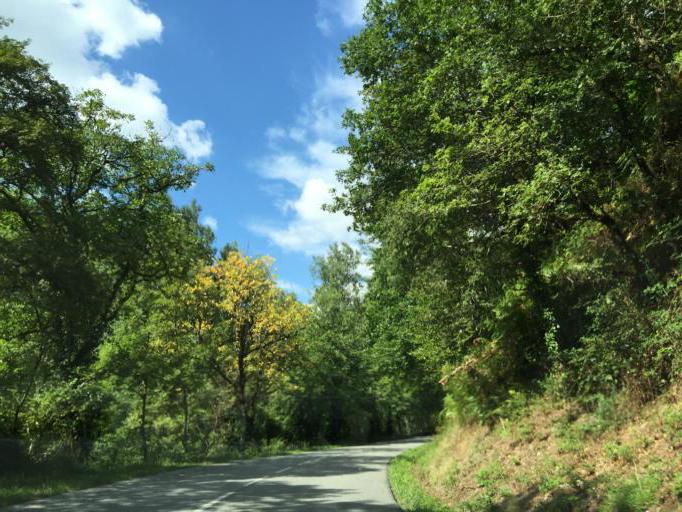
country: FR
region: Midi-Pyrenees
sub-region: Departement de l'Aveyron
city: Saint-Christophe-Vallon
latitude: 44.5624
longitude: 2.4087
